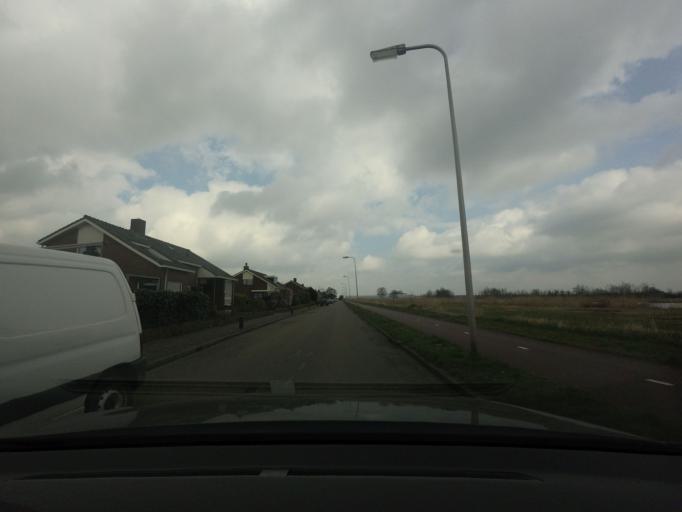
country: NL
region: Utrecht
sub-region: Gemeente De Ronde Venen
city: Mijdrecht
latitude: 52.1665
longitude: 4.8295
